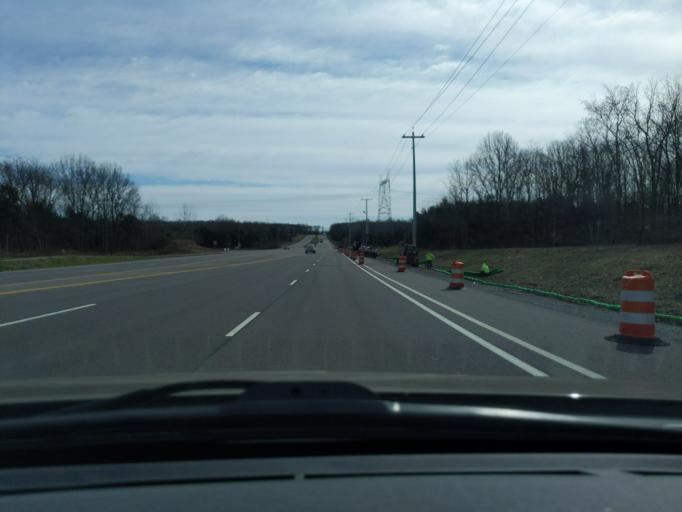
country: US
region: Tennessee
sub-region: Wilson County
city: Mount Juliet
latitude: 36.1865
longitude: -86.4656
